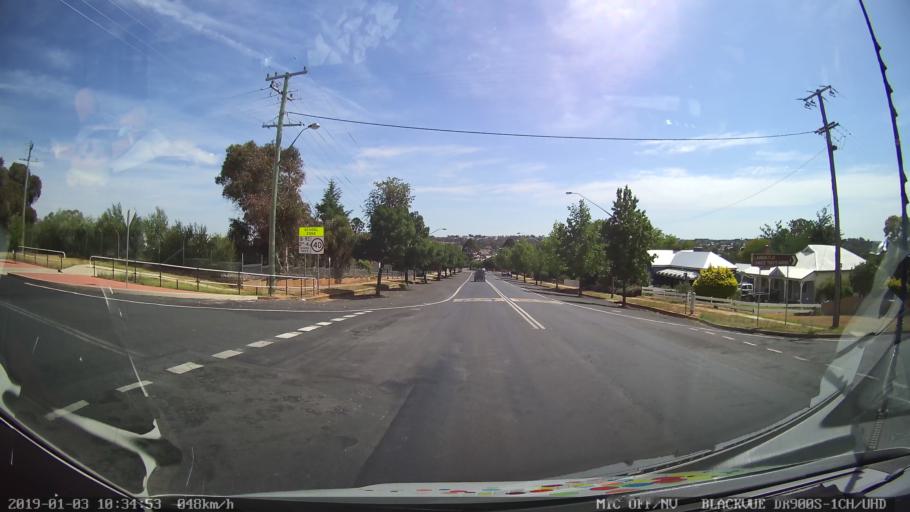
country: AU
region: New South Wales
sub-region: Young
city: Young
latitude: -34.3188
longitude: 148.2925
